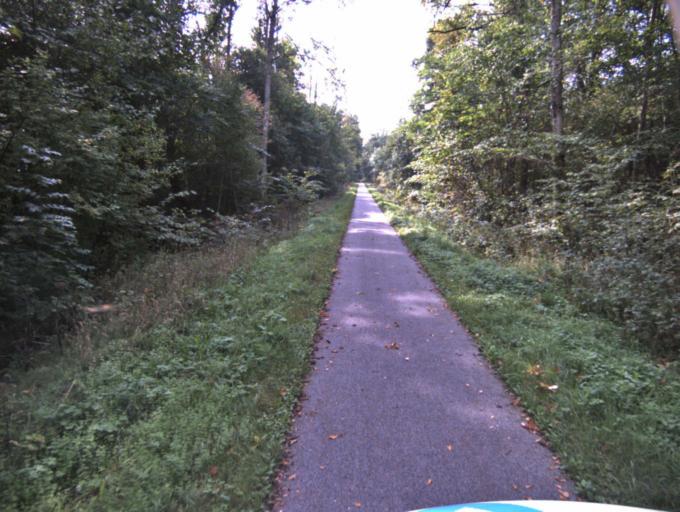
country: SE
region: Vaestra Goetaland
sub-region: Tranemo Kommun
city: Limmared
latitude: 57.6514
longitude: 13.3611
